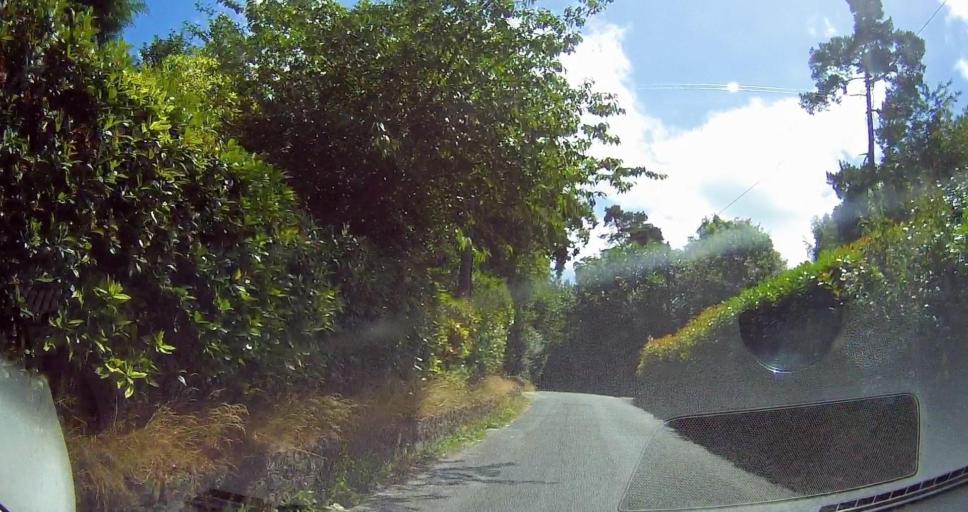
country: GB
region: England
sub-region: Kent
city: Borough Green
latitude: 51.2878
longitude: 0.3124
